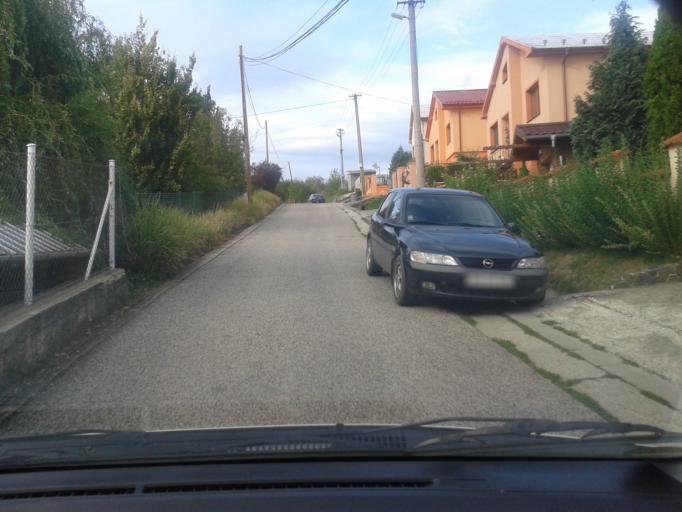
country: SK
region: Nitriansky
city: Zlate Moravce
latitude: 48.3946
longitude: 18.3577
